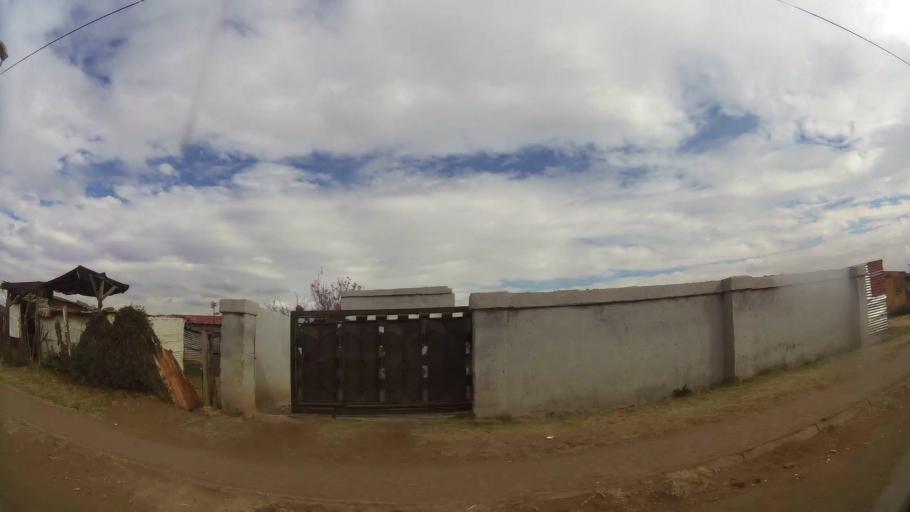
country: ZA
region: Gauteng
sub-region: Ekurhuleni Metropolitan Municipality
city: Germiston
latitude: -26.4054
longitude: 28.1506
